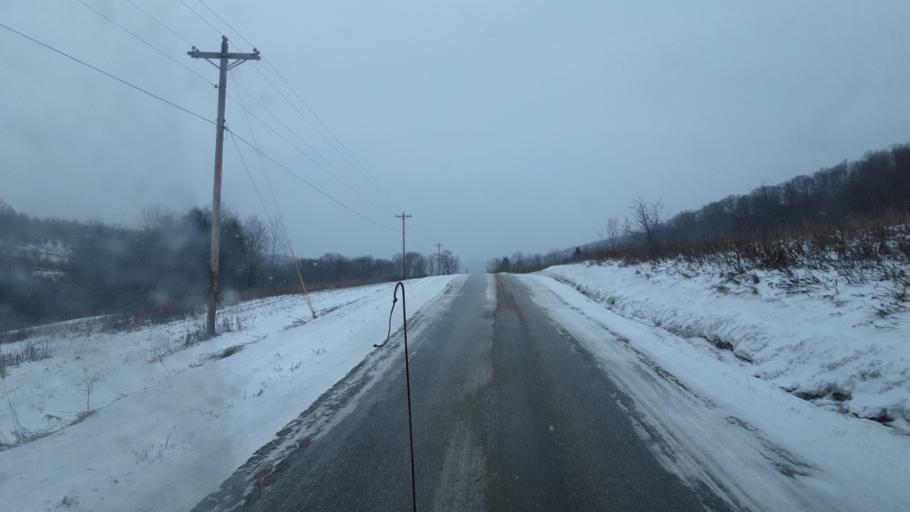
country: US
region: Pennsylvania
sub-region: Tioga County
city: Westfield
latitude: 41.9661
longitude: -77.7156
